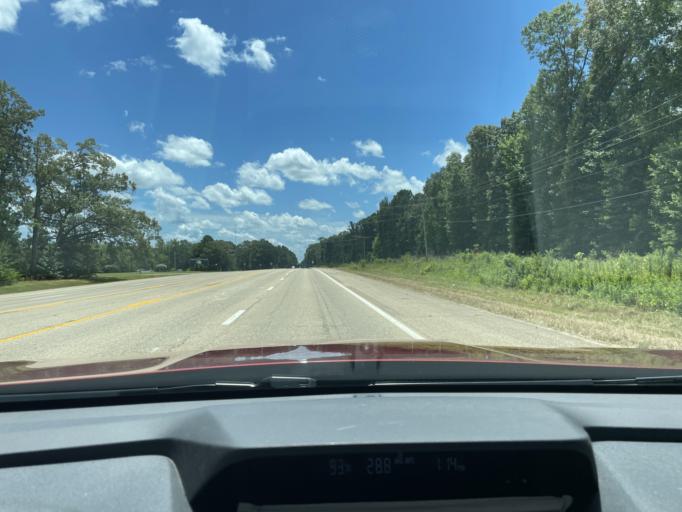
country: US
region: Arkansas
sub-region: Drew County
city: Monticello
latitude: 33.6614
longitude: -91.8033
